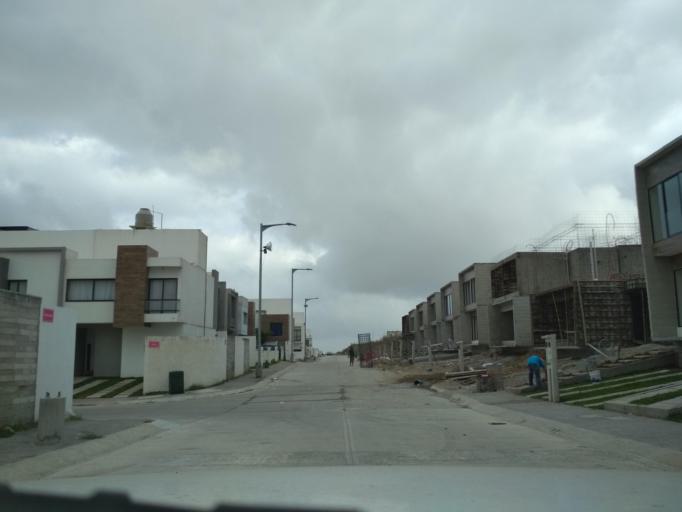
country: MX
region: Veracruz
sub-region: Veracruz
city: Fraccionamiento Geovillas los Pinos
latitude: 19.2154
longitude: -96.2325
